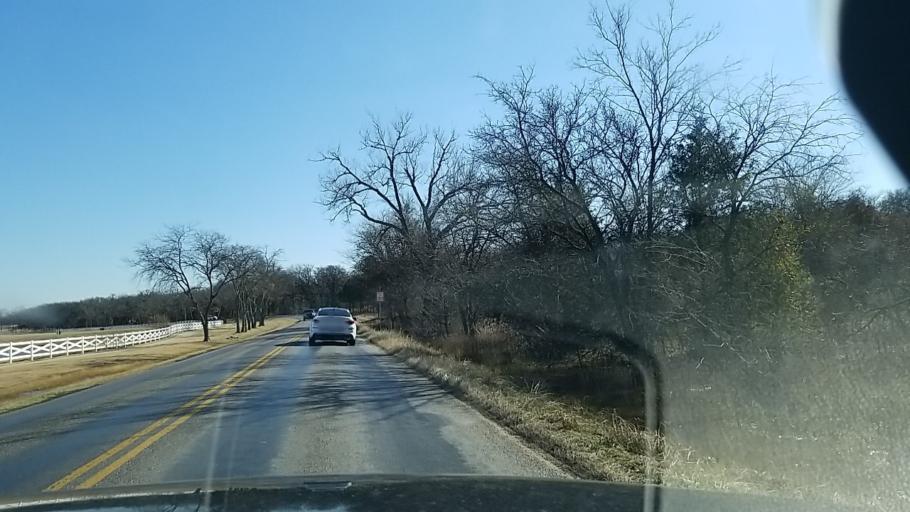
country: US
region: Texas
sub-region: Denton County
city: Argyle
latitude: 33.1298
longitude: -97.1941
